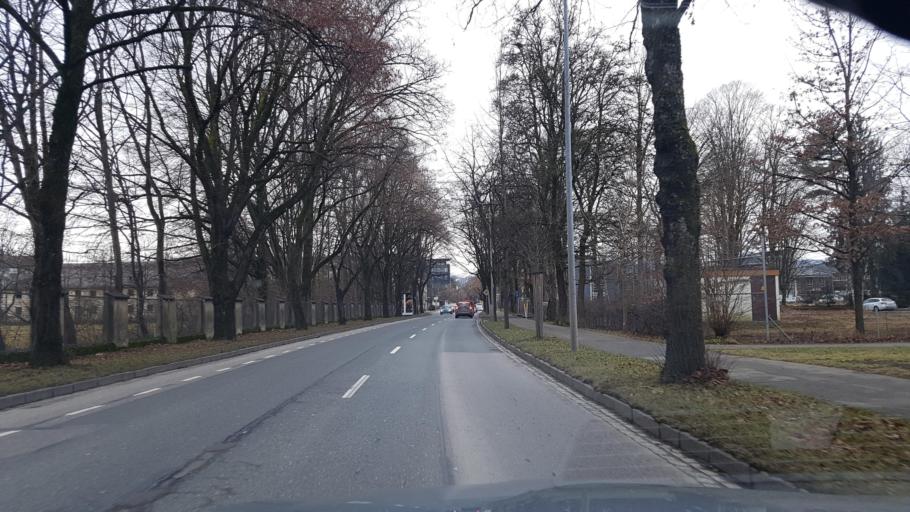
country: DE
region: Bavaria
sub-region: Upper Bavaria
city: Rosenheim
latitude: 47.8685
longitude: 12.1106
